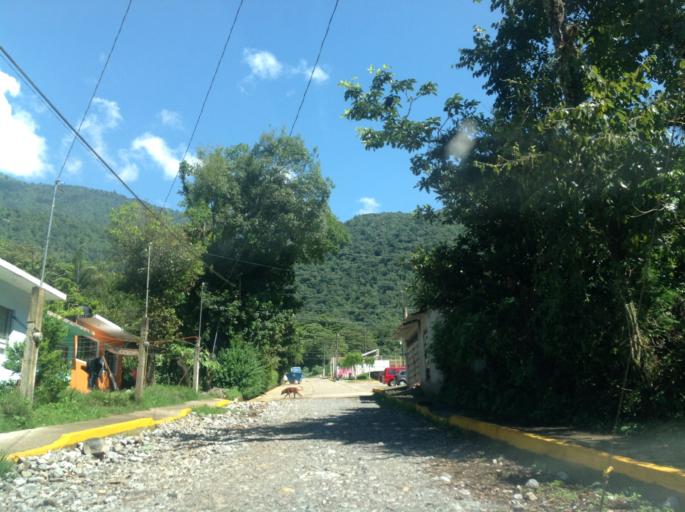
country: MX
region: Veracruz
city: Nogales
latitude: 18.8428
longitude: -97.1581
